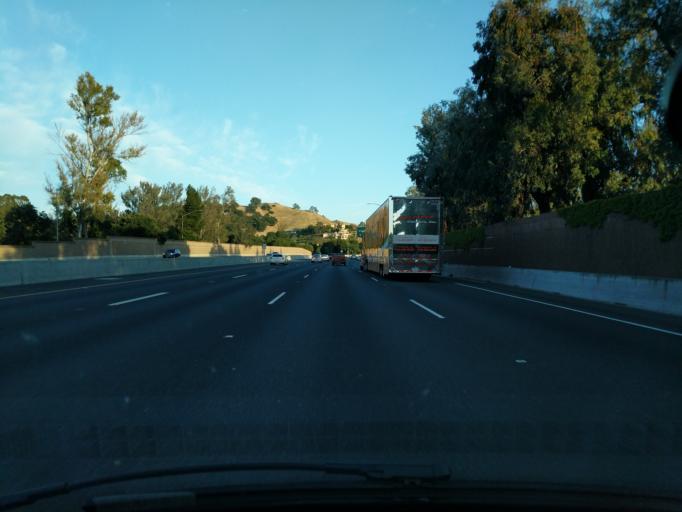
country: US
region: California
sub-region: Contra Costa County
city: Alamo
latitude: 37.8564
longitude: -122.0304
